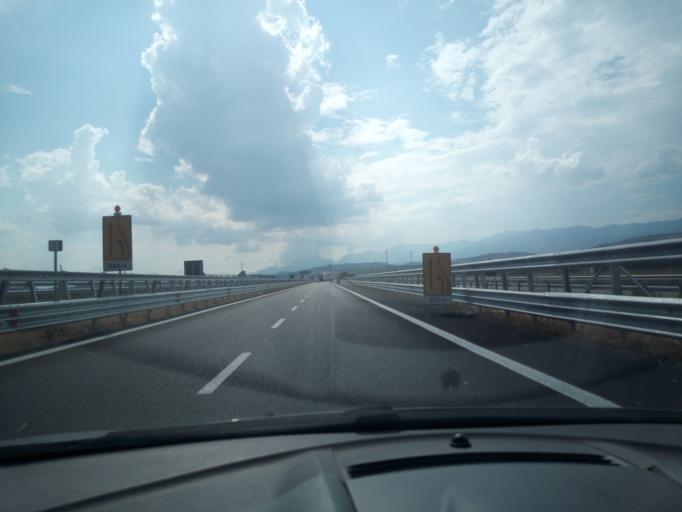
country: IT
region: Calabria
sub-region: Provincia di Cosenza
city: San Lorenzo del Vallo
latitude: 39.7244
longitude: 16.2563
